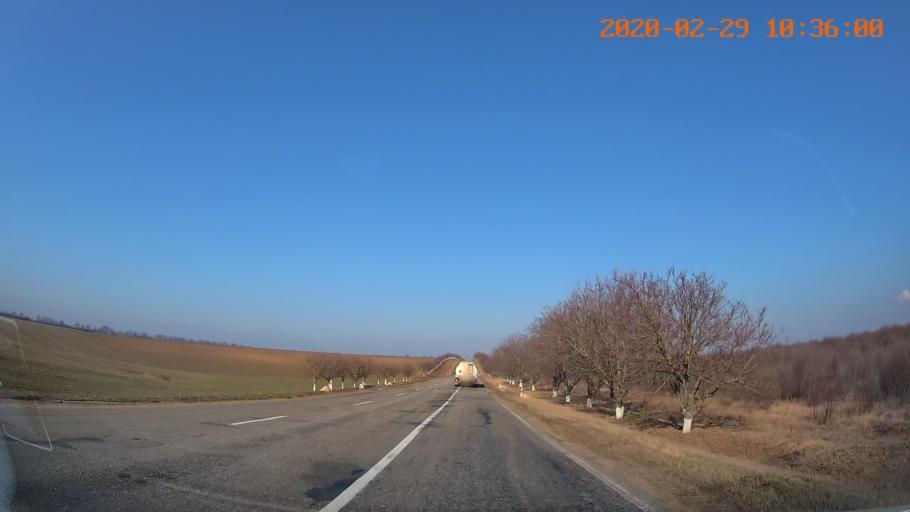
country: MD
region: Anenii Noi
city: Varnita
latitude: 46.9911
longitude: 29.5122
